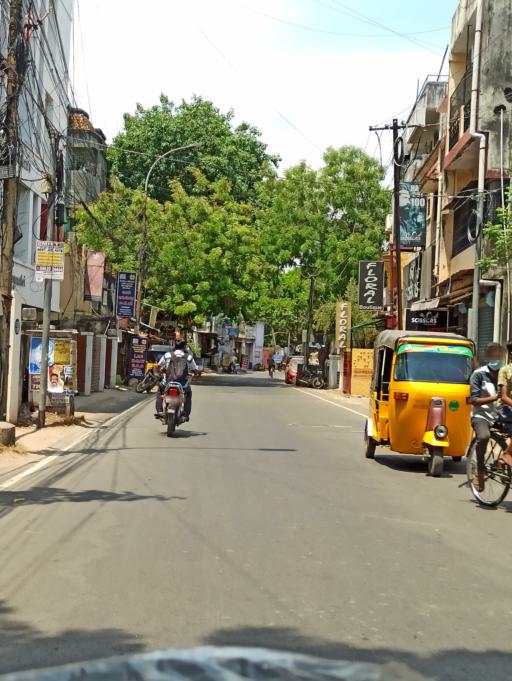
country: IN
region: Tamil Nadu
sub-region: Chennai
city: Chetput
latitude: 13.0587
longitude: 80.2300
